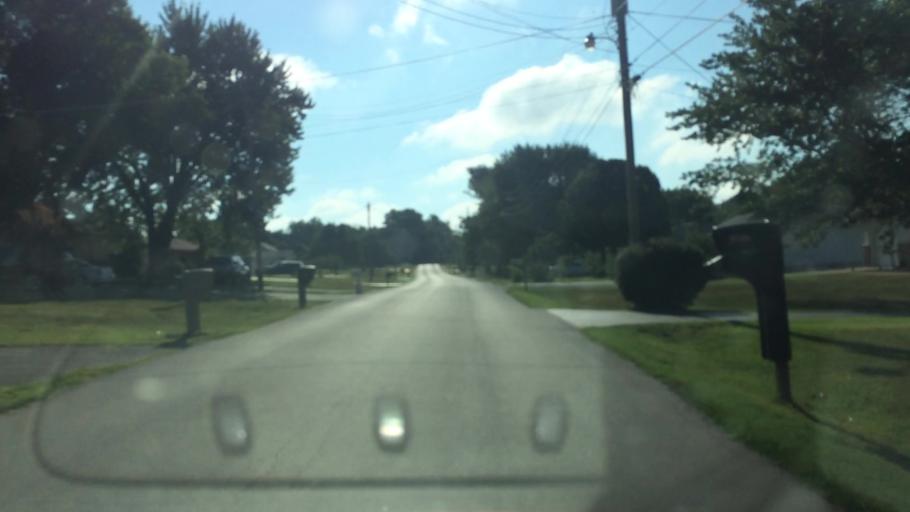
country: US
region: Missouri
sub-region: Greene County
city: Springfield
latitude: 37.2595
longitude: -93.2769
